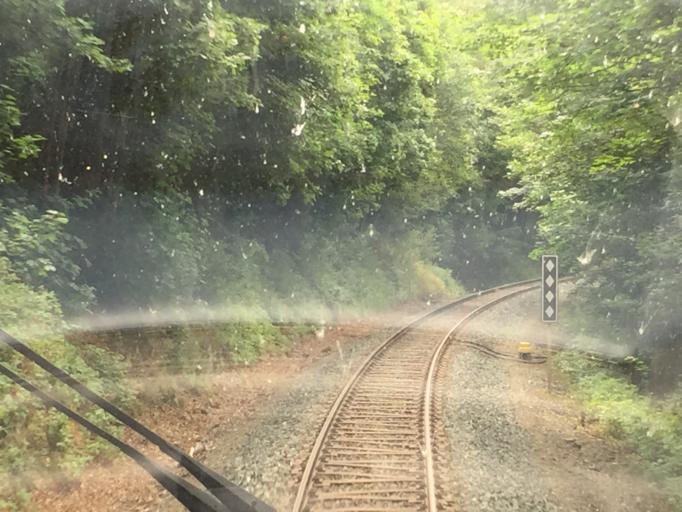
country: DE
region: Hesse
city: Willingen
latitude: 51.2892
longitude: 8.6197
